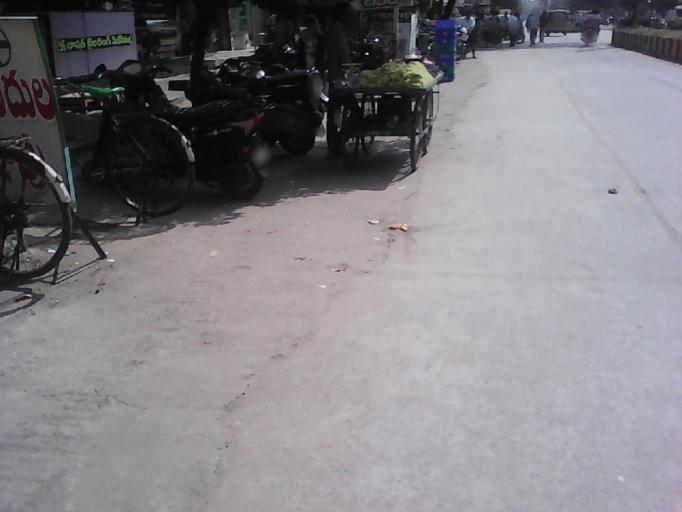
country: IN
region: Andhra Pradesh
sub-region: Guntur
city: Bhattiprolu
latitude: 16.2373
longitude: 80.6489
